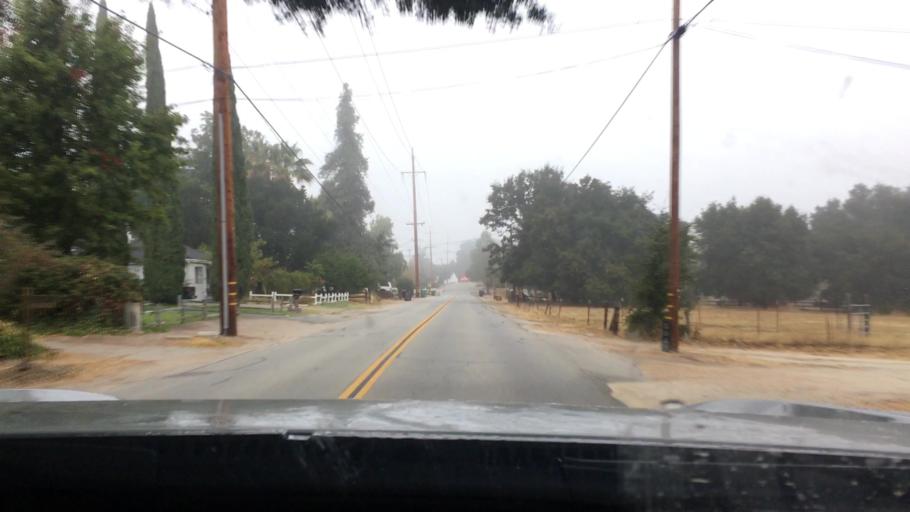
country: US
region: California
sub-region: San Luis Obispo County
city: Atascadero
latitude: 35.4867
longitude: -120.6856
